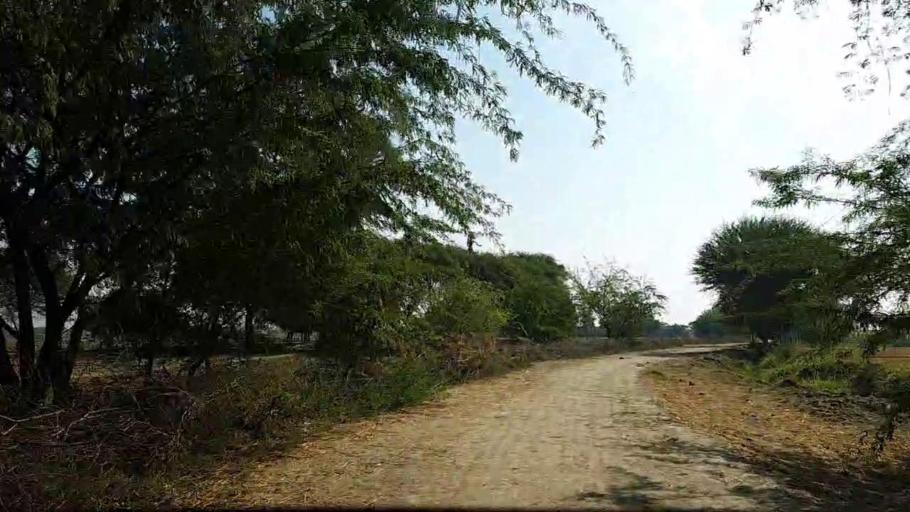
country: PK
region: Sindh
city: Daro Mehar
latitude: 24.7656
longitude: 68.1330
